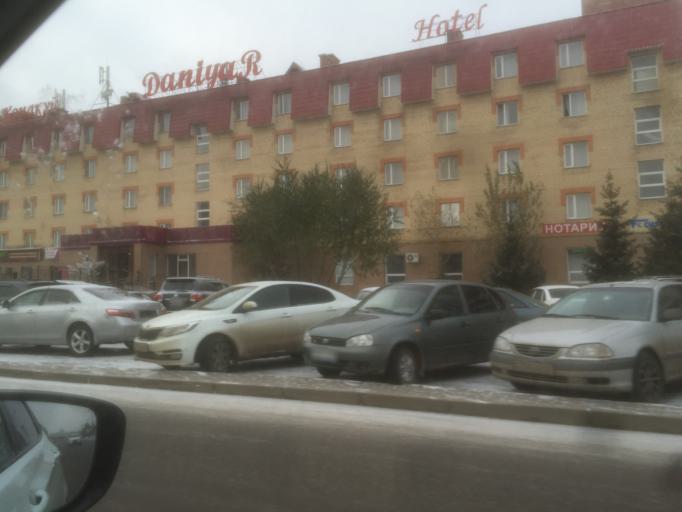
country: KZ
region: Astana Qalasy
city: Astana
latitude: 51.1497
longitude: 71.4570
